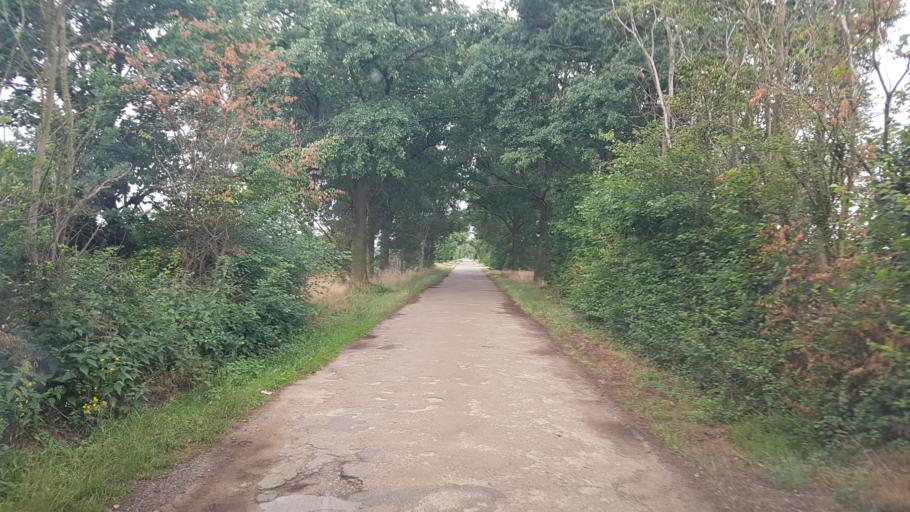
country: DE
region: Saxony-Anhalt
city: Annaburg
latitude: 51.7604
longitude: 13.0179
